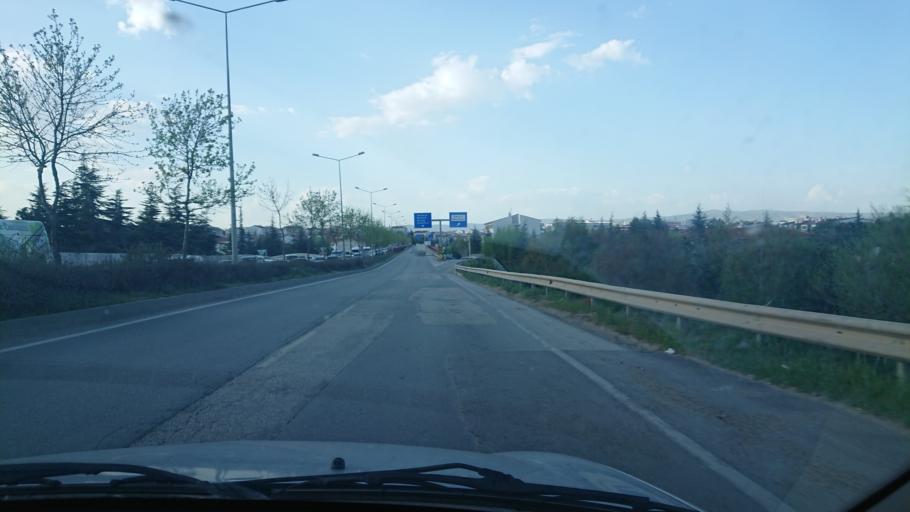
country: TR
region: Eskisehir
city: Eskisehir
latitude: 39.7763
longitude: 30.4841
